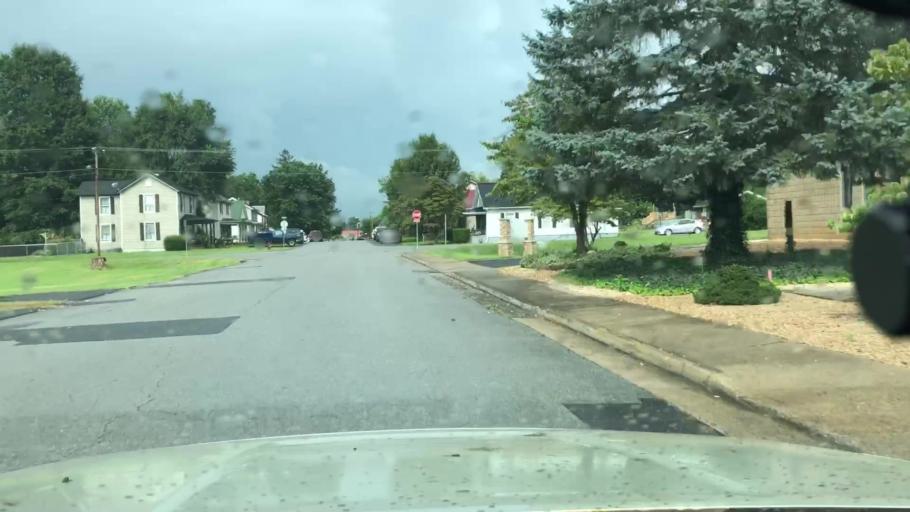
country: US
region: Virginia
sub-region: City of Waynesboro
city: Waynesboro
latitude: 38.0694
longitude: -78.9019
